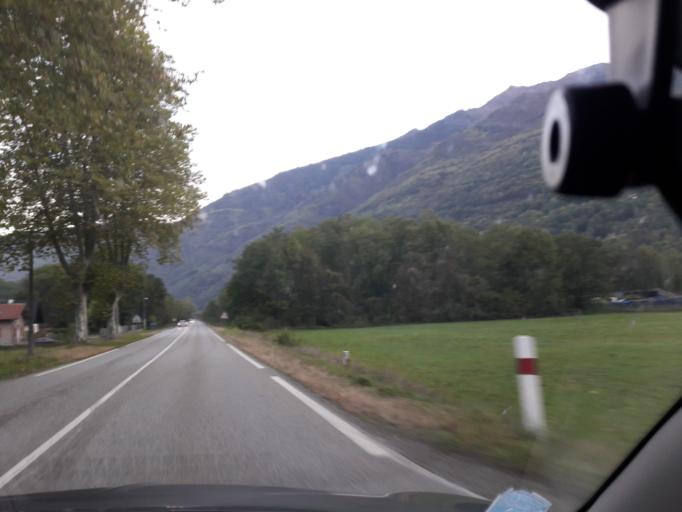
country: FR
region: Rhone-Alpes
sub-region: Departement de la Savoie
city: Aiton
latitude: 45.5265
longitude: 6.3118
